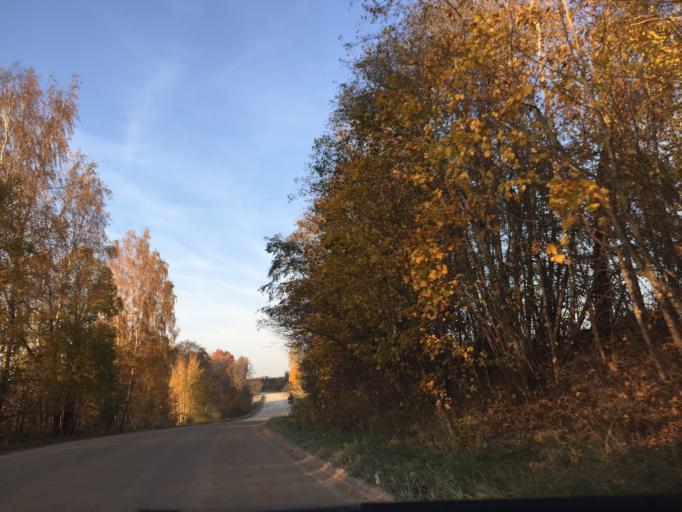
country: LV
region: Vainode
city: Vainode
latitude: 56.5129
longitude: 21.8289
